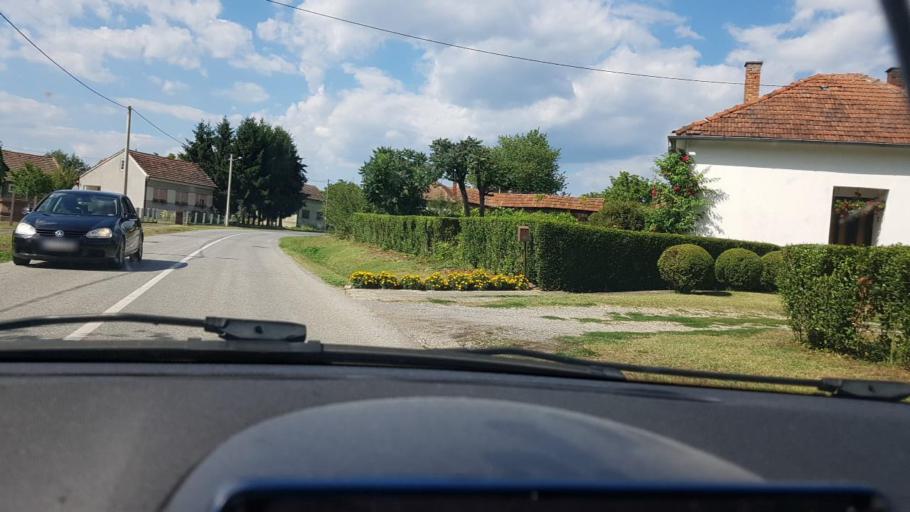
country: HR
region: Bjelovarsko-Bilogorska
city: Zdralovi
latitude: 45.8450
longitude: 16.9733
